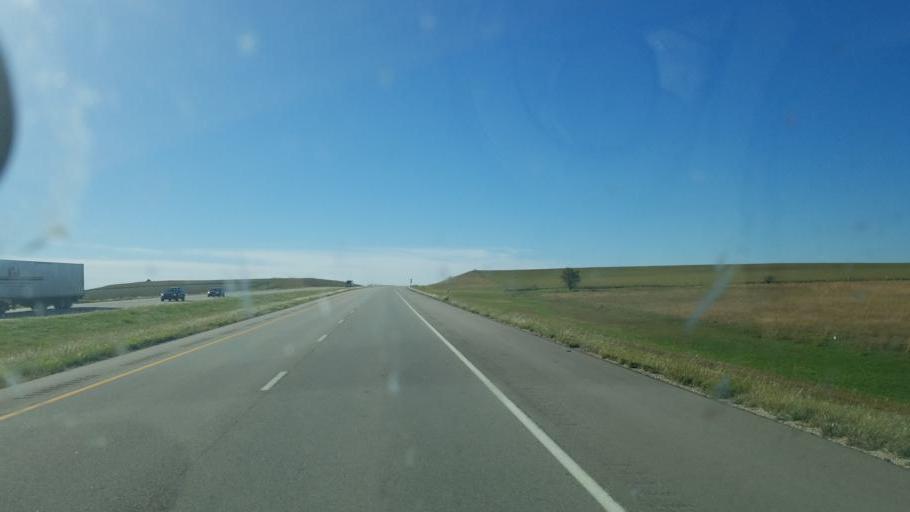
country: US
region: Kansas
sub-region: Ellsworth County
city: Ellsworth
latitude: 38.8494
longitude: -98.5013
